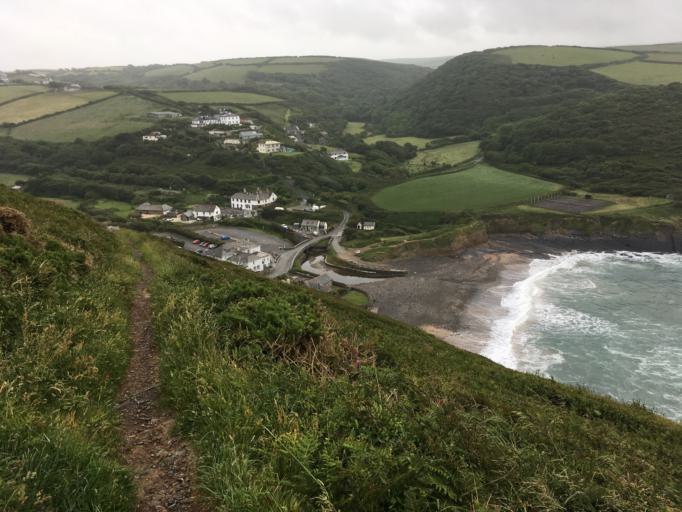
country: GB
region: England
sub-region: Cornwall
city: Jacobstow
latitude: 50.7433
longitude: -4.6339
